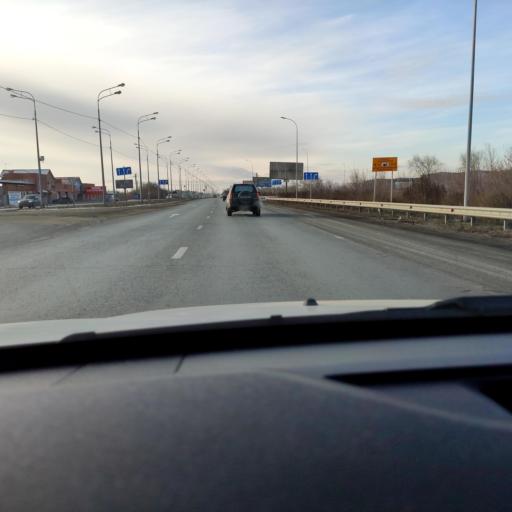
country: RU
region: Samara
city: Smyshlyayevka
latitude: 53.2646
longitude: 50.3866
